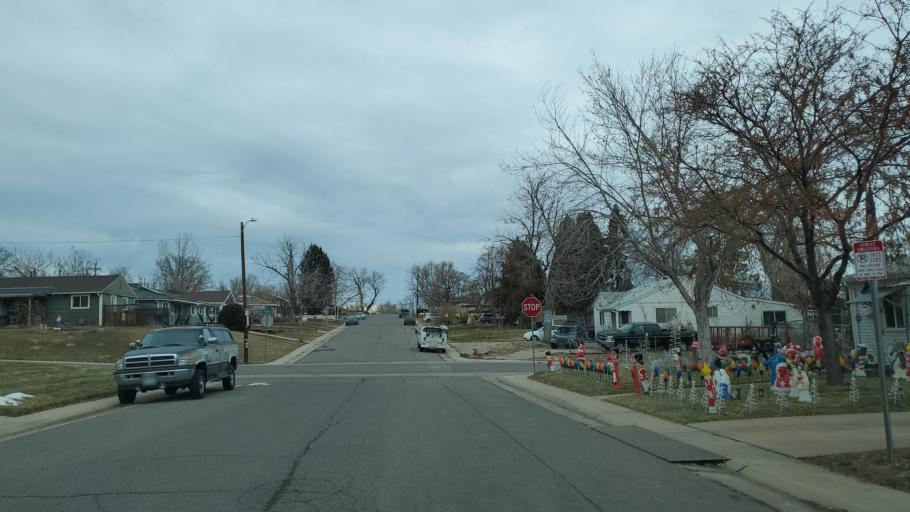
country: US
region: Colorado
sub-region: Denver County
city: Denver
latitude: 39.7016
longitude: -105.0041
